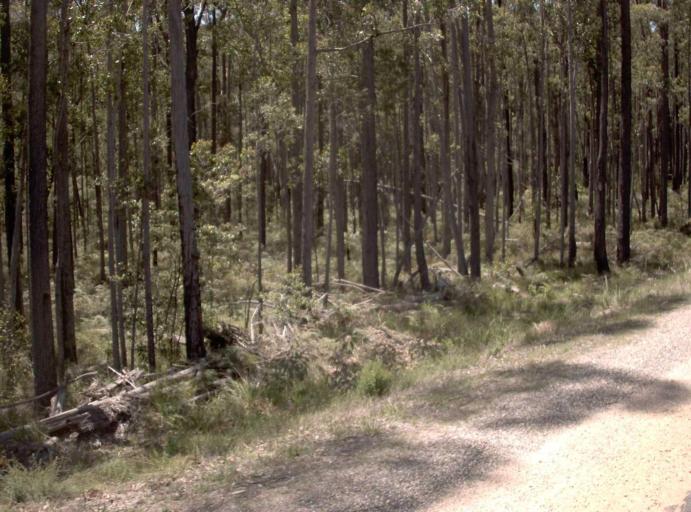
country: AU
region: Victoria
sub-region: East Gippsland
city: Lakes Entrance
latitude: -37.6716
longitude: 148.7955
